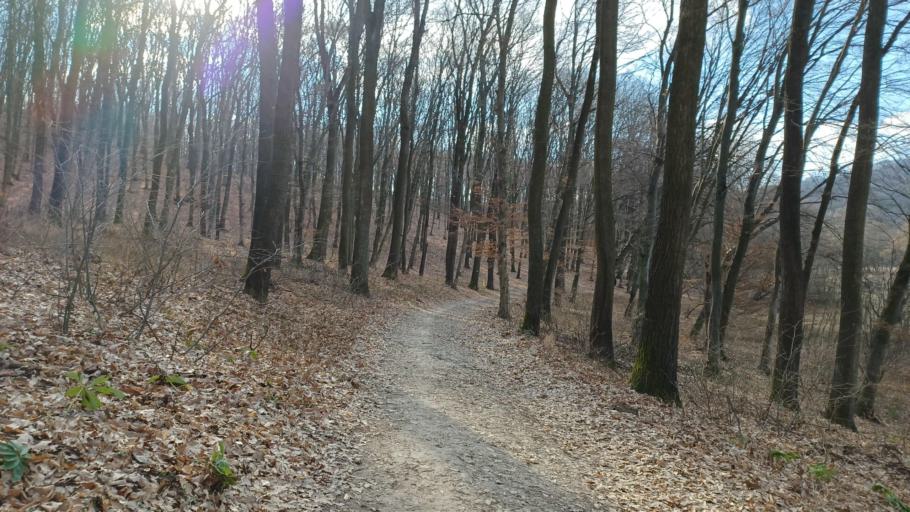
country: HU
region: Tolna
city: Szentgalpuszta
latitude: 46.3394
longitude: 18.6229
